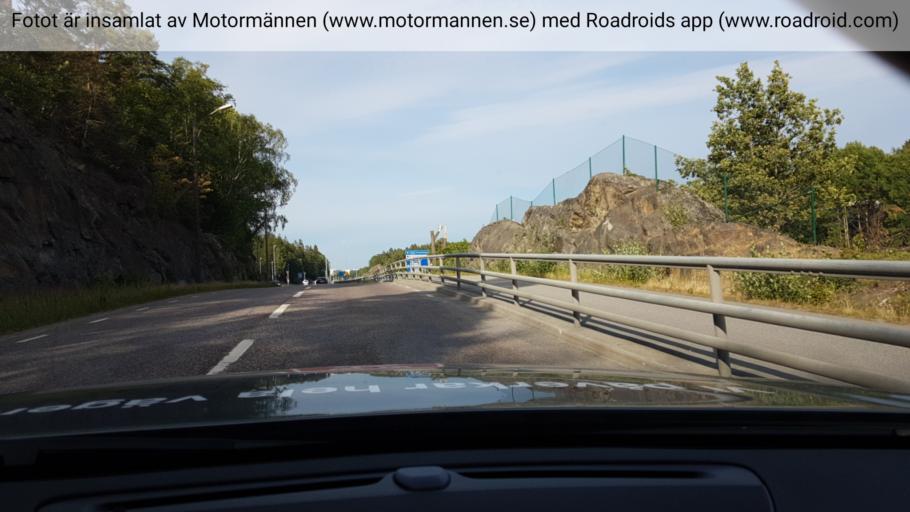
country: SE
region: Stockholm
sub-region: Botkyrka Kommun
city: Tullinge
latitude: 59.2083
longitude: 17.9134
